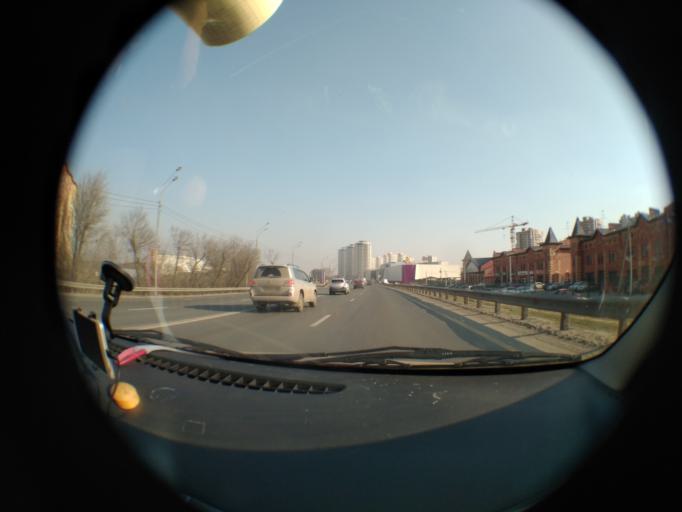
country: RU
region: Moskovskaya
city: Oktyabr'skiy
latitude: 55.6028
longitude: 37.9808
